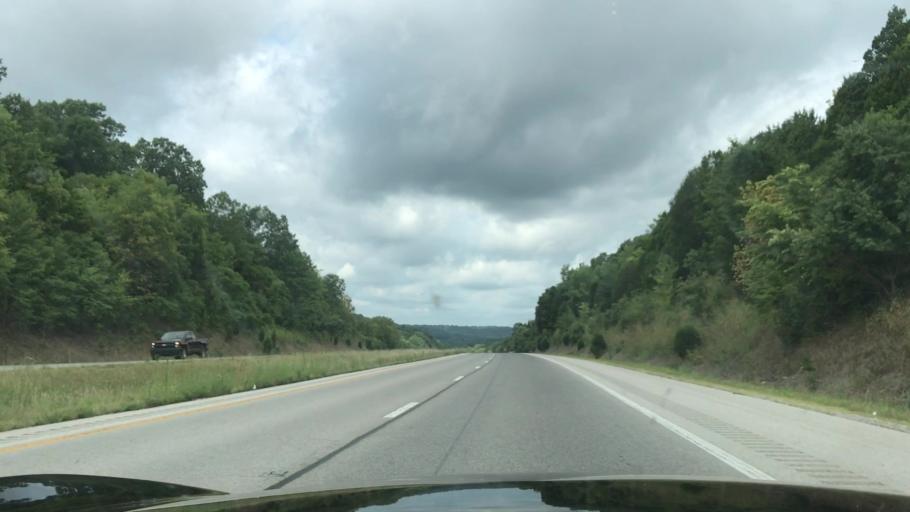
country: US
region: Kentucky
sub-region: Warren County
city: Bowling Green
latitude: 37.0351
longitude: -86.5472
